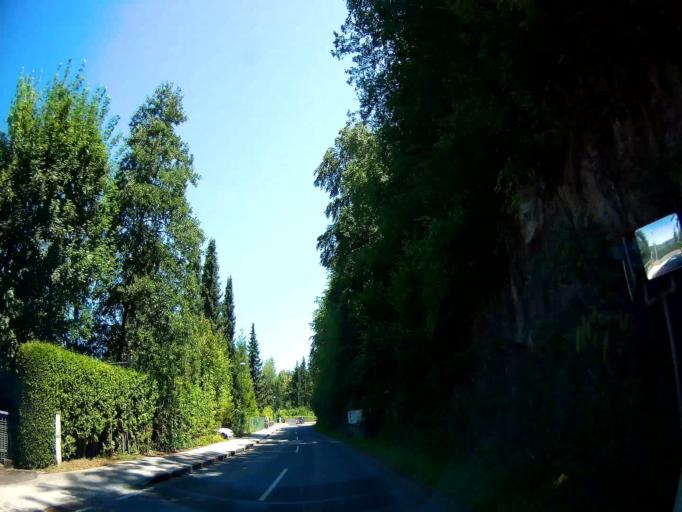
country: AT
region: Carinthia
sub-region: Politischer Bezirk Klagenfurt Land
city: Keutschach am See
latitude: 46.6092
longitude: 14.2026
